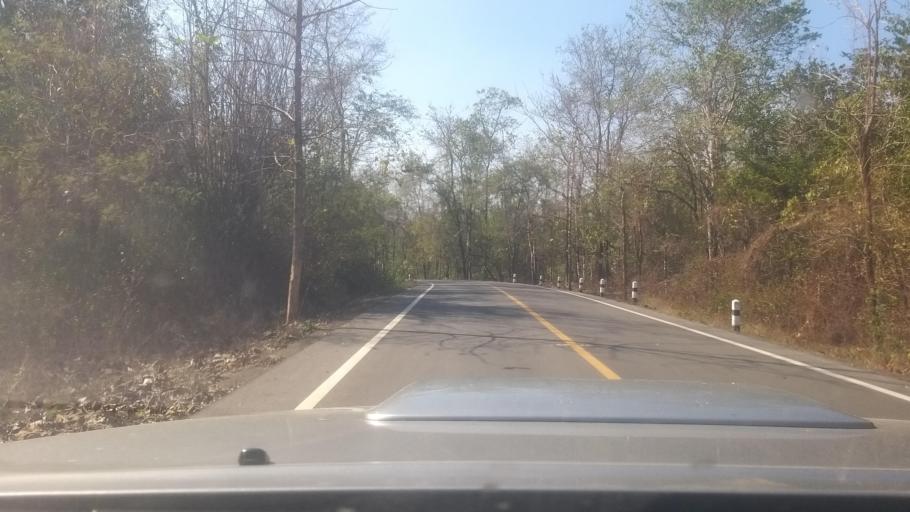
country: TH
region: Phrae
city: Nong Muang Khai
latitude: 18.2951
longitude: 100.0568
